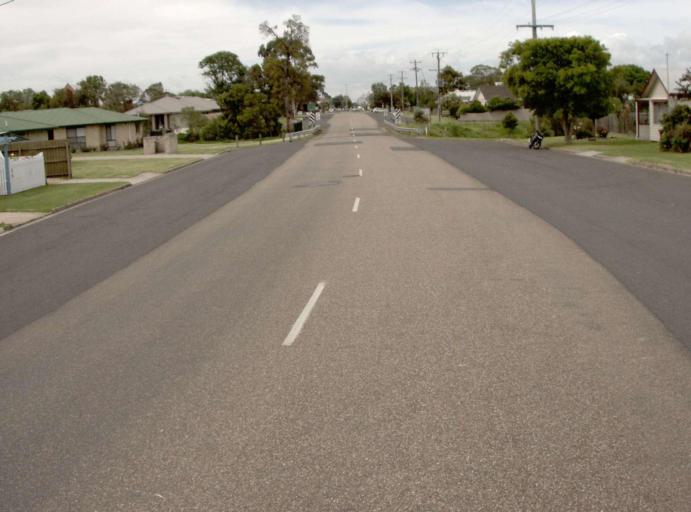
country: AU
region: Victoria
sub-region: Wellington
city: Sale
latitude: -37.9604
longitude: 147.0812
